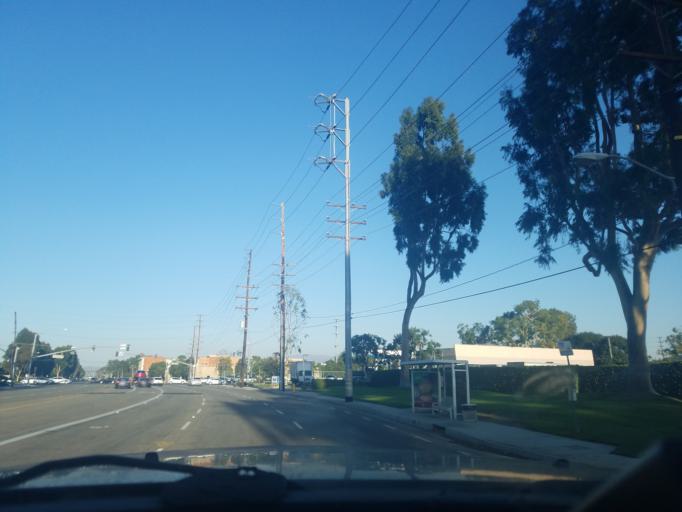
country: US
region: California
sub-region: Orange County
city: Irvine
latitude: 33.6930
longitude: -117.8559
